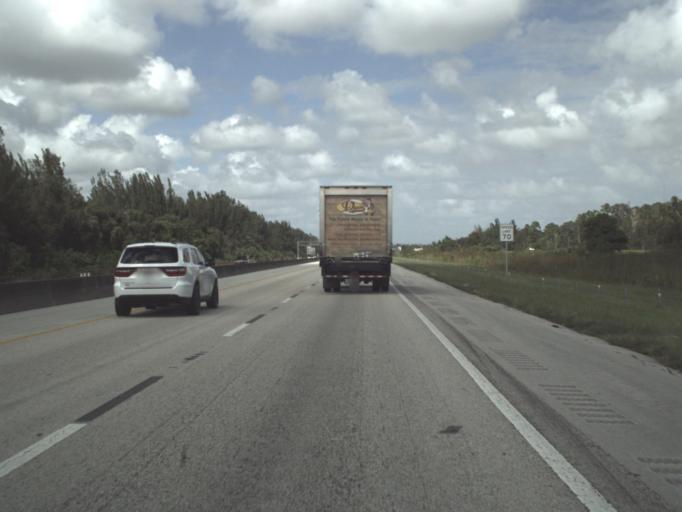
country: US
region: Florida
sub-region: Palm Beach County
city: Plantation Mobile Home Park
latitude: 26.7229
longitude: -80.1356
